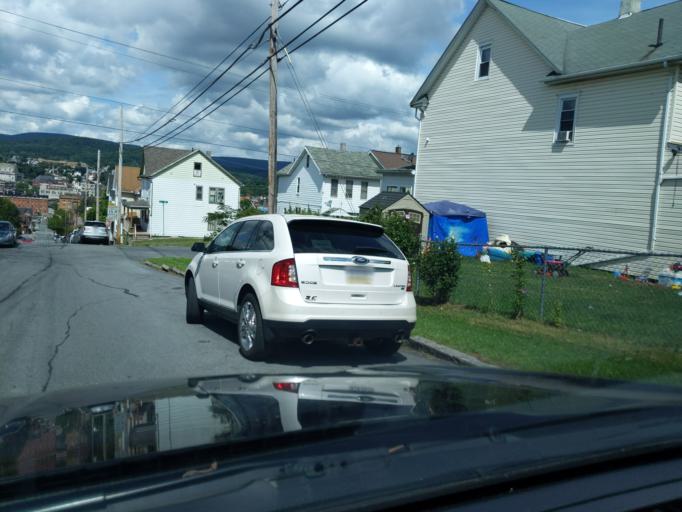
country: US
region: Pennsylvania
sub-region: Blair County
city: Altoona
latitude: 40.5110
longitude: -78.3930
